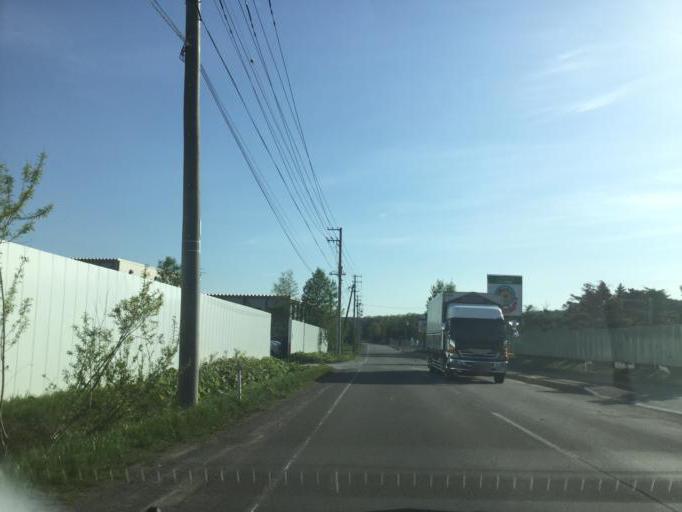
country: JP
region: Hokkaido
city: Kitahiroshima
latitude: 43.0063
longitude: 141.5534
